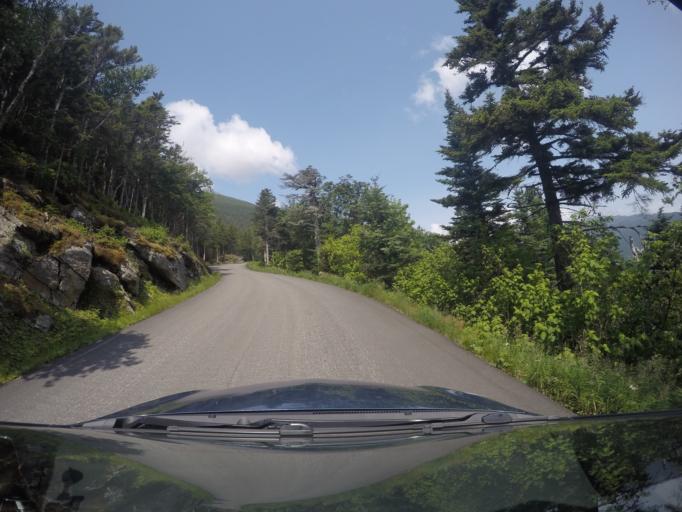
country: US
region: New Hampshire
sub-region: Coos County
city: Gorham
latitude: 44.2831
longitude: -71.2578
